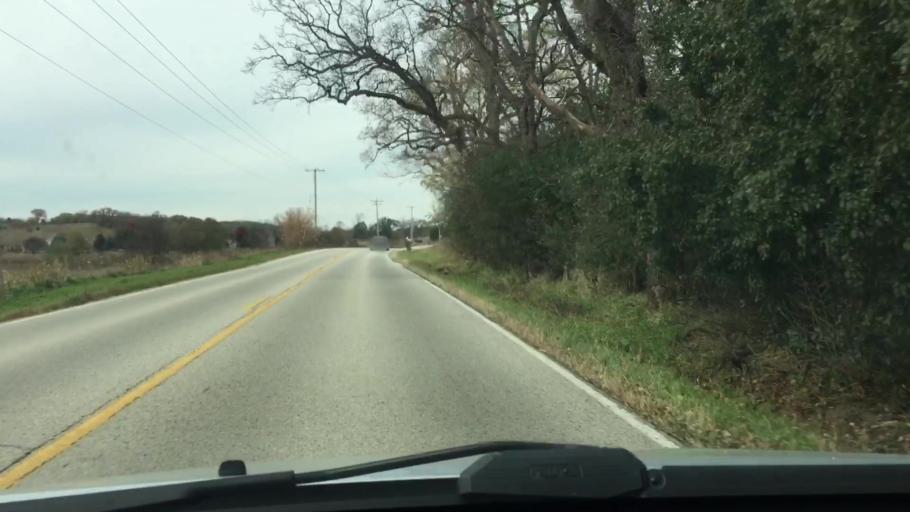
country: US
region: Wisconsin
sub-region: Waukesha County
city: Mukwonago
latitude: 42.8846
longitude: -88.3726
